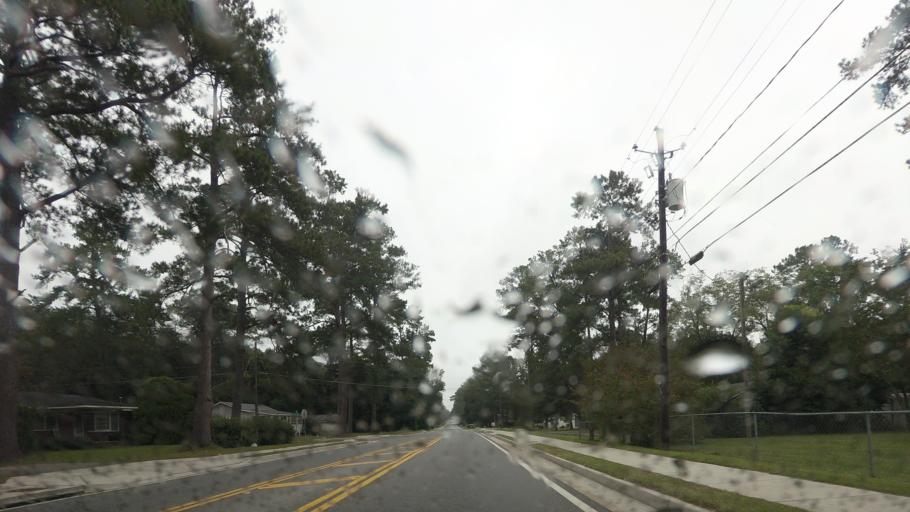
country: US
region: Georgia
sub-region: Lowndes County
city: Remerton
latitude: 30.8293
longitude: -83.3070
